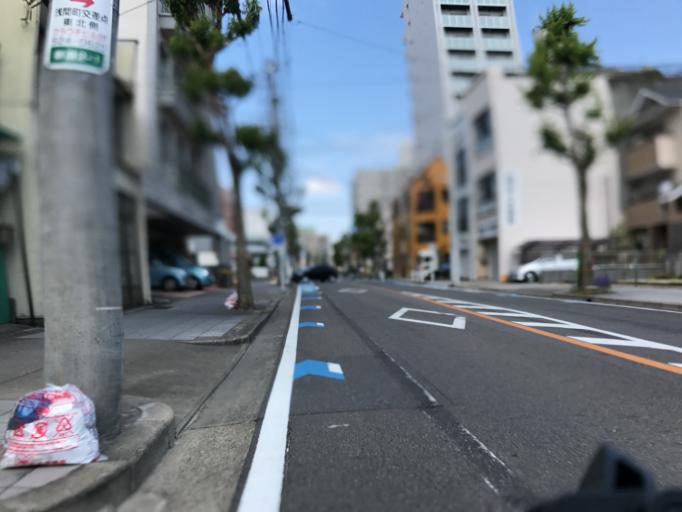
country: JP
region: Aichi
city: Nagoya-shi
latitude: 35.1802
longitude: 136.8892
